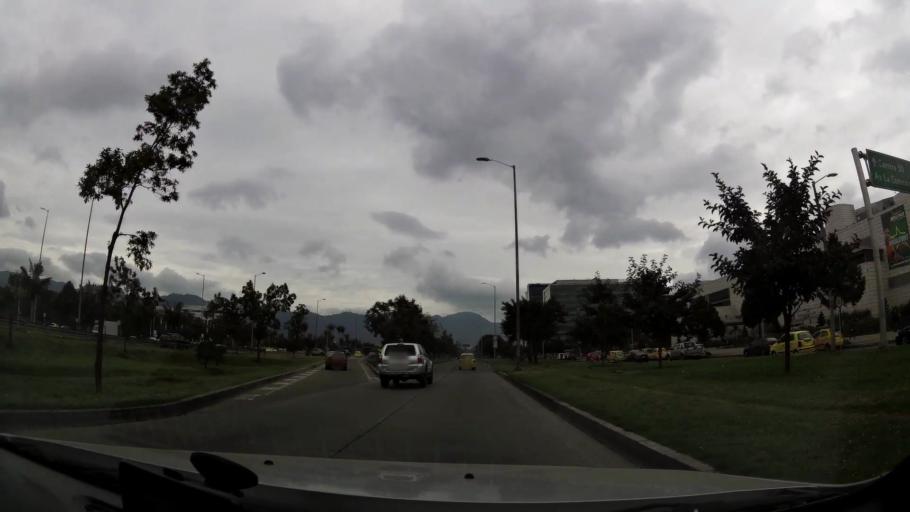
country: CO
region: Bogota D.C.
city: Bogota
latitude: 4.6485
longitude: -74.1006
